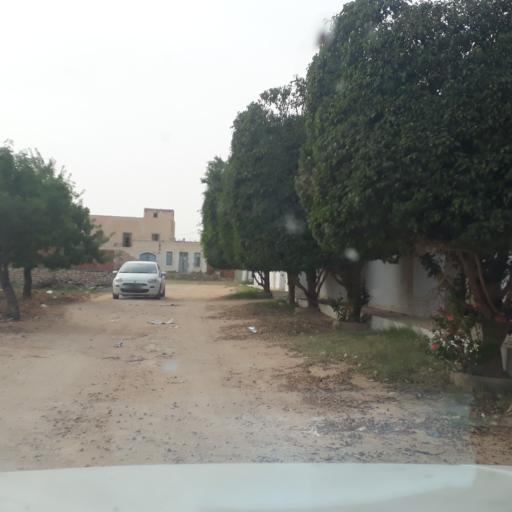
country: TN
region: Safaqis
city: Al Qarmadah
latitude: 34.8205
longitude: 10.7775
